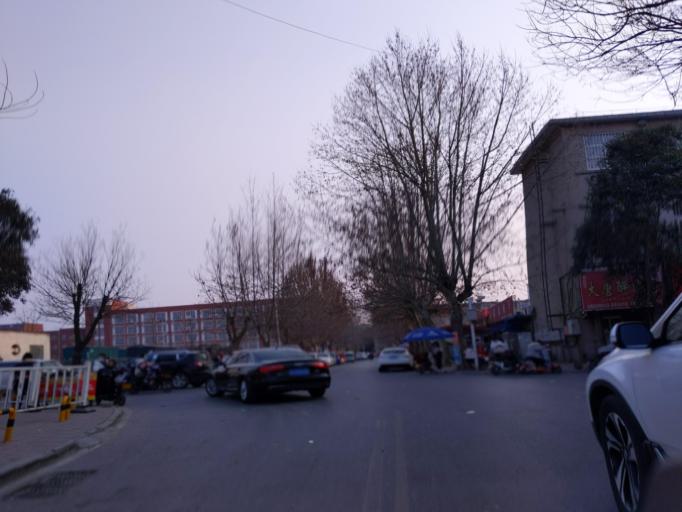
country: CN
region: Henan Sheng
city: Zhongyuanlu
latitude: 35.7846
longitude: 115.0636
